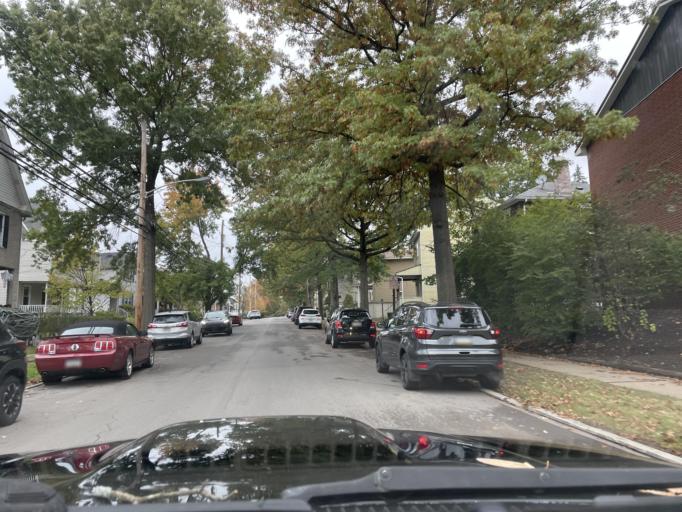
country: US
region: Pennsylvania
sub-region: Allegheny County
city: Oakmont
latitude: 40.5221
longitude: -79.8388
